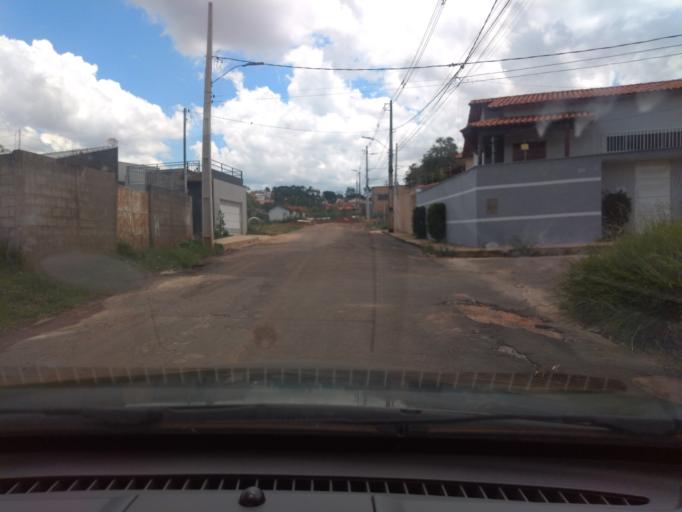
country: BR
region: Minas Gerais
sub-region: Tres Coracoes
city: Tres Coracoes
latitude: -21.6698
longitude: -45.2700
